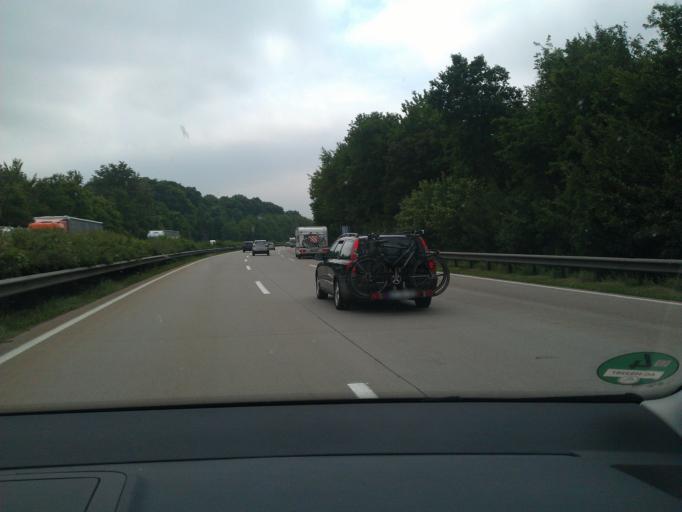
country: DE
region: Rheinland-Pfalz
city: Waldorf
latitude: 50.4985
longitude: 7.2251
